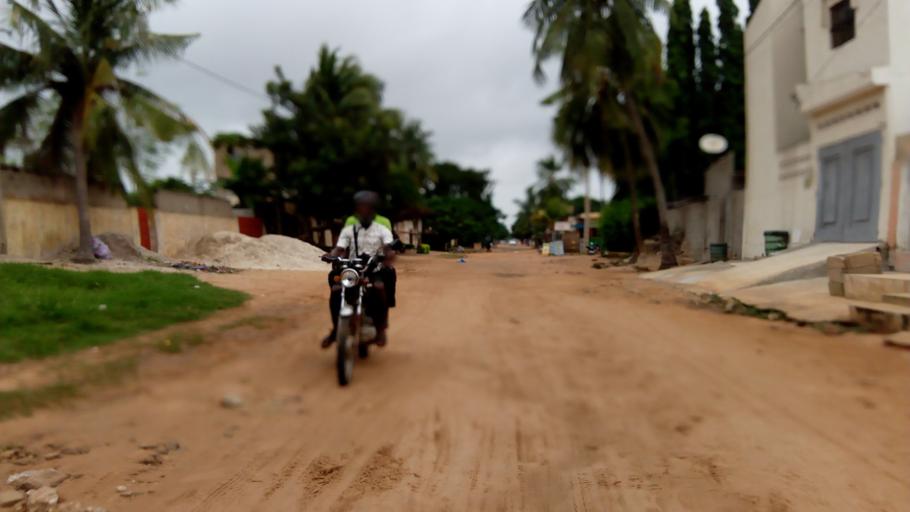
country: TG
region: Maritime
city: Lome
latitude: 6.1790
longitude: 1.1782
